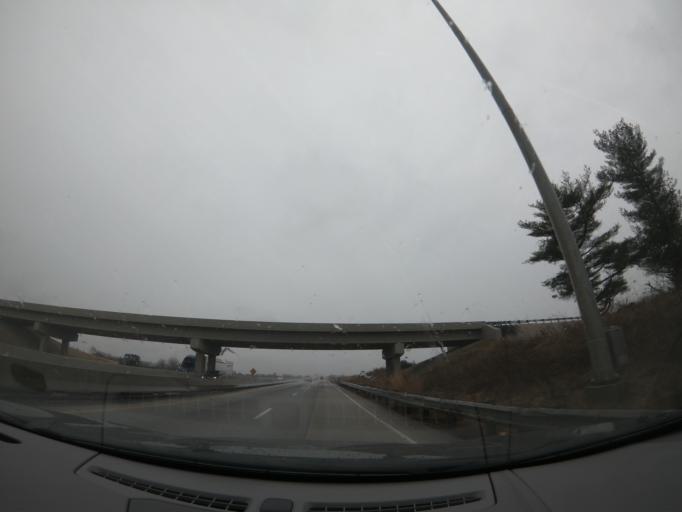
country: US
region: Kentucky
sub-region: Larue County
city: Hodgenville
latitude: 37.5541
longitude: -85.8780
